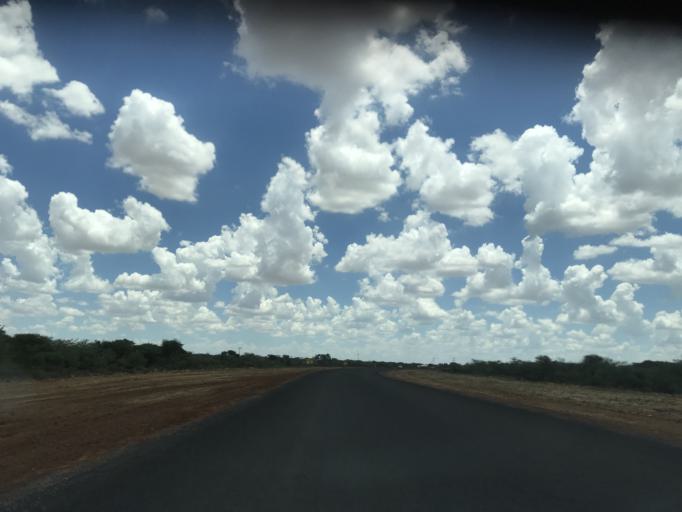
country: BW
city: Mabuli
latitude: -25.8054
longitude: 24.6795
